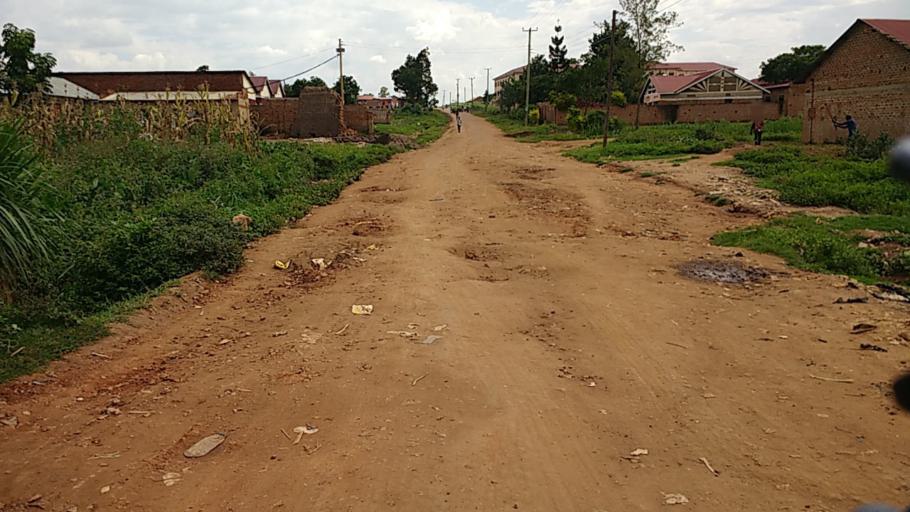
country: UG
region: Eastern Region
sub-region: Mbale District
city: Mbale
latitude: 1.0843
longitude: 34.1623
